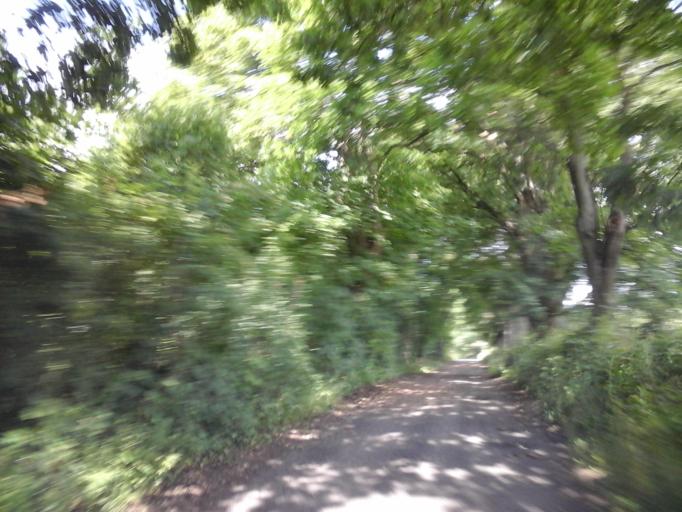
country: PL
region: West Pomeranian Voivodeship
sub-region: Powiat choszczenski
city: Recz
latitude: 53.2893
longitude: 15.5936
